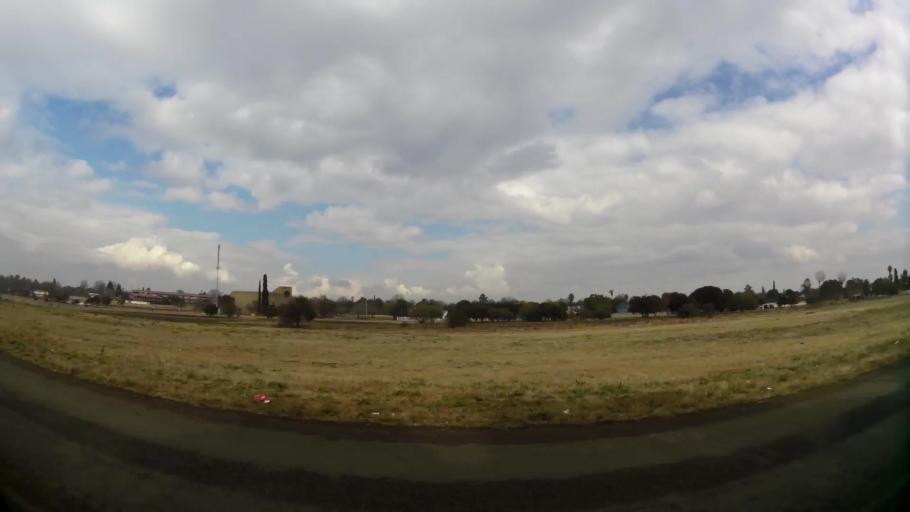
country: ZA
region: Gauteng
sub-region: Sedibeng District Municipality
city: Vanderbijlpark
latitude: -26.7121
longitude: 27.8524
